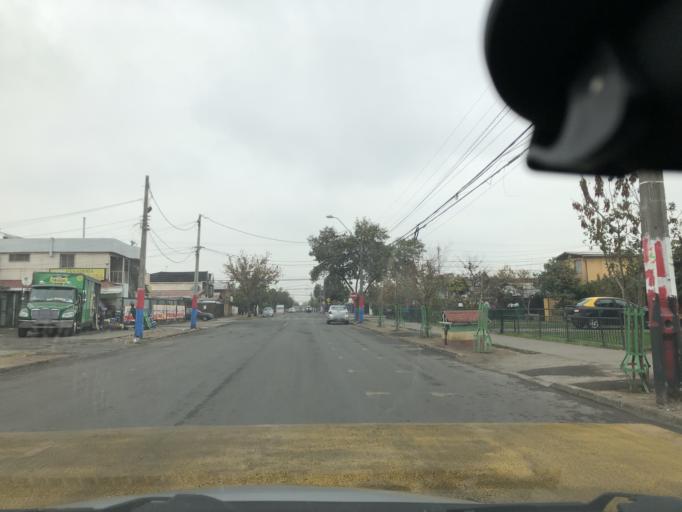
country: CL
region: Santiago Metropolitan
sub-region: Provincia de Cordillera
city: Puente Alto
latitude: -33.5827
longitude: -70.5912
